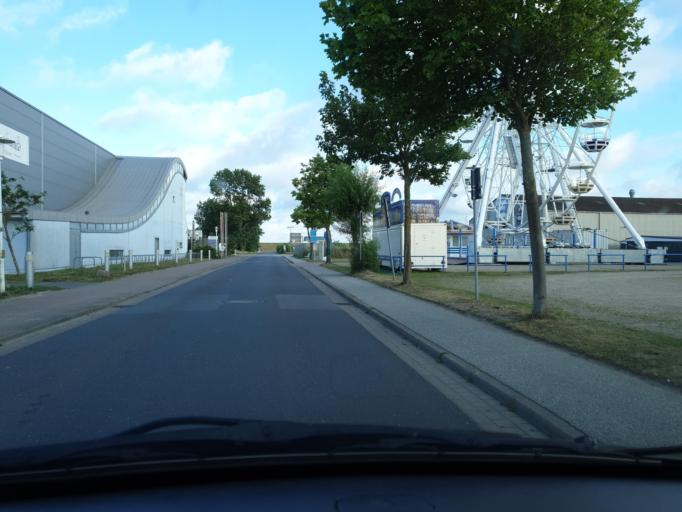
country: DE
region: Schleswig-Holstein
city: Busum
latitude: 54.1287
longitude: 8.8689
